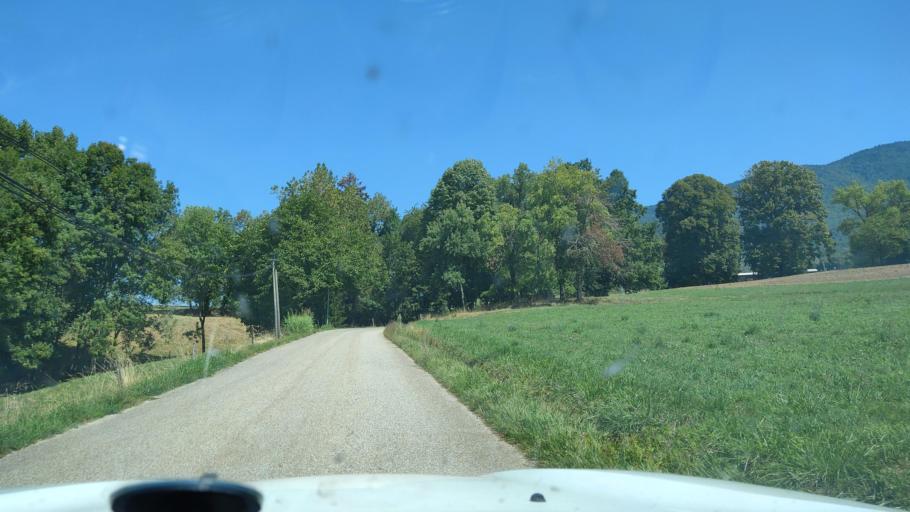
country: FR
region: Rhone-Alpes
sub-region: Departement de la Savoie
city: Novalaise
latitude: 45.6394
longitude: 5.7740
